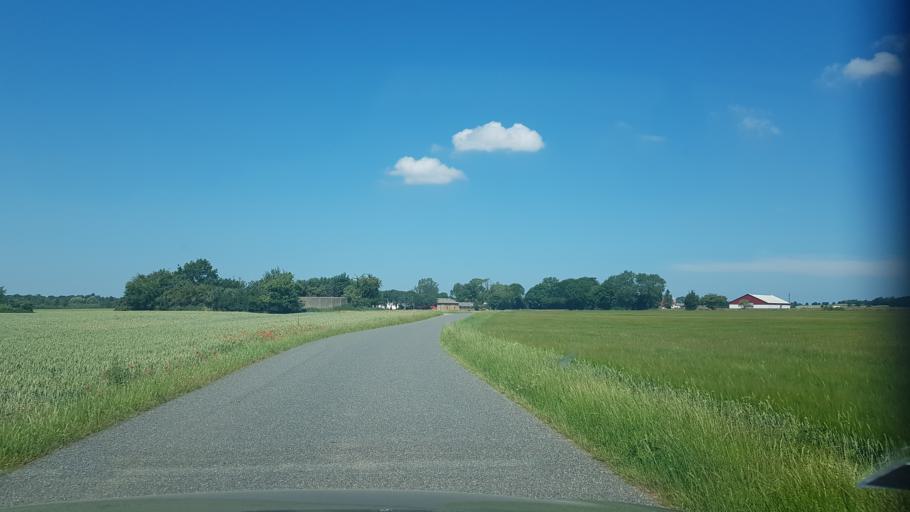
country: DK
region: Zealand
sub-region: Kalundborg Kommune
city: Svebolle
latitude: 55.6955
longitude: 11.2978
